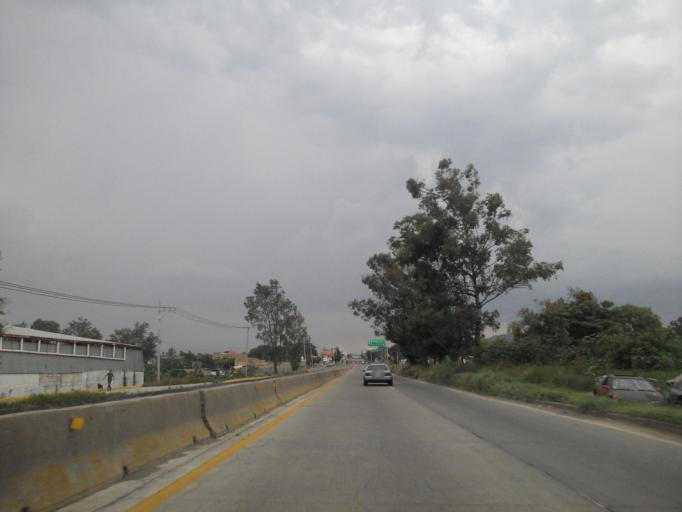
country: MX
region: Jalisco
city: Tonala
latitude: 20.5995
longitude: -103.2336
